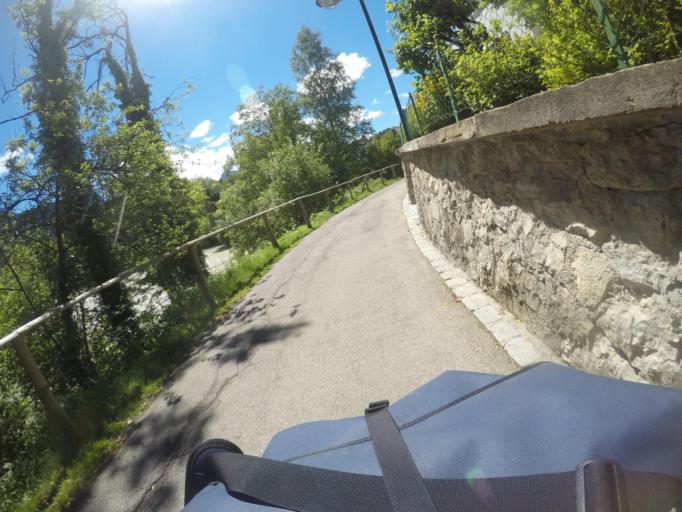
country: DE
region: Bavaria
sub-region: Swabia
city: Fuessen
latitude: 47.5659
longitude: 10.6958
